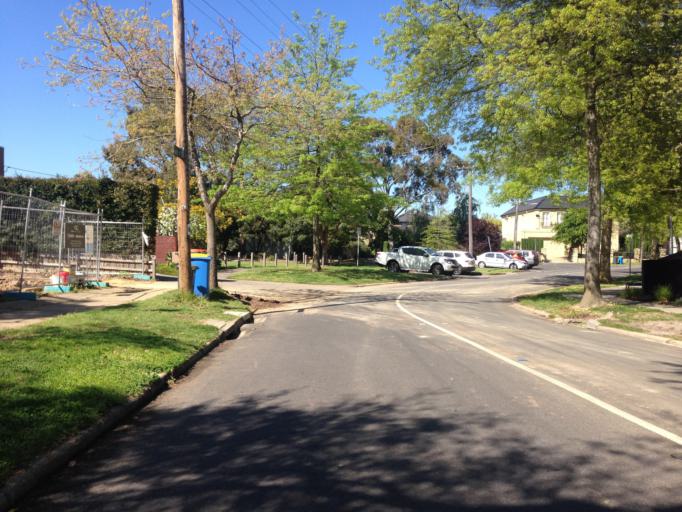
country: AU
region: Victoria
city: Balwyn
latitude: -37.8054
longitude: 145.0686
